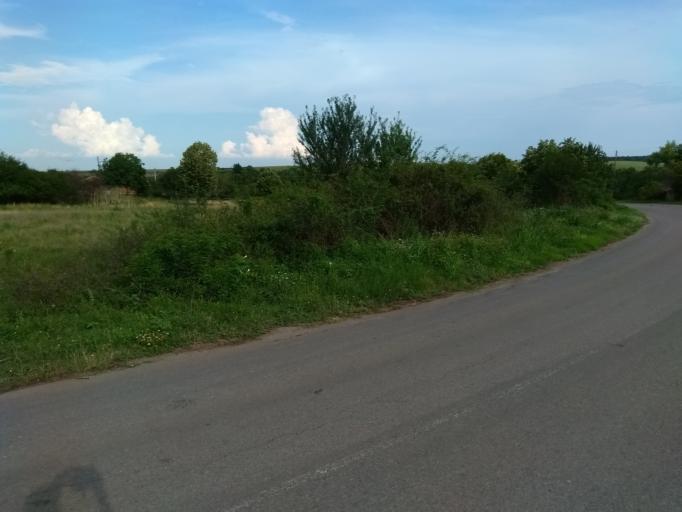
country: BG
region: Sliven
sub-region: Obshtina Sliven
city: Kermen
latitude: 42.4532
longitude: 26.1426
